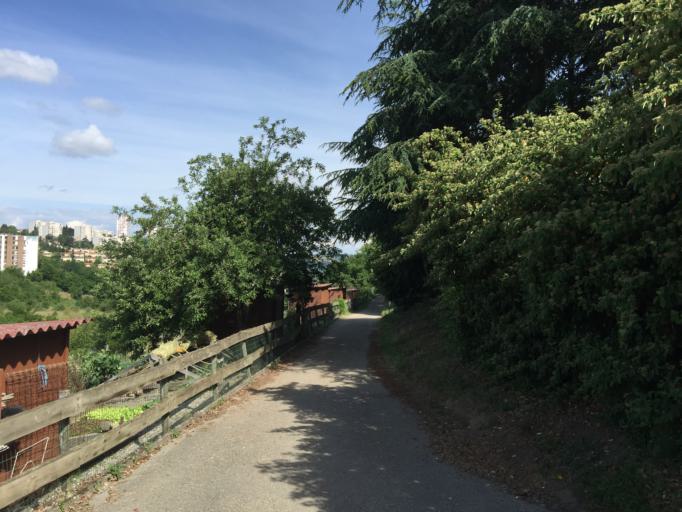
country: FR
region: Rhone-Alpes
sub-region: Departement de la Loire
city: Saint-Priest-en-Jarez
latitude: 45.4599
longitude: 4.3730
